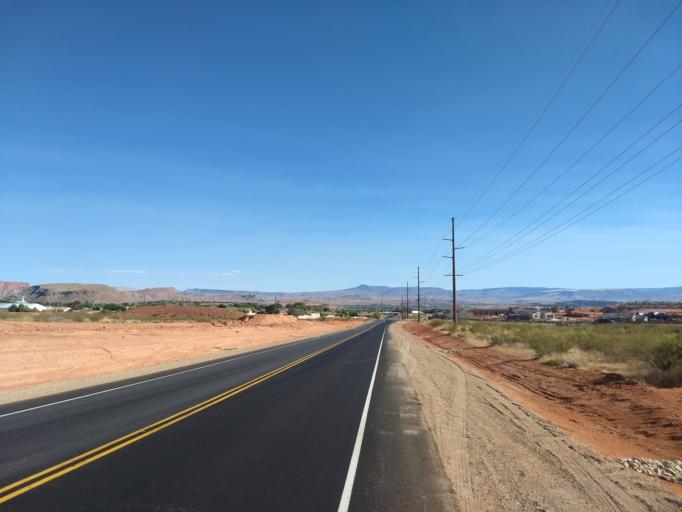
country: US
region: Utah
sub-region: Washington County
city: Washington
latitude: 37.1465
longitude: -113.5098
